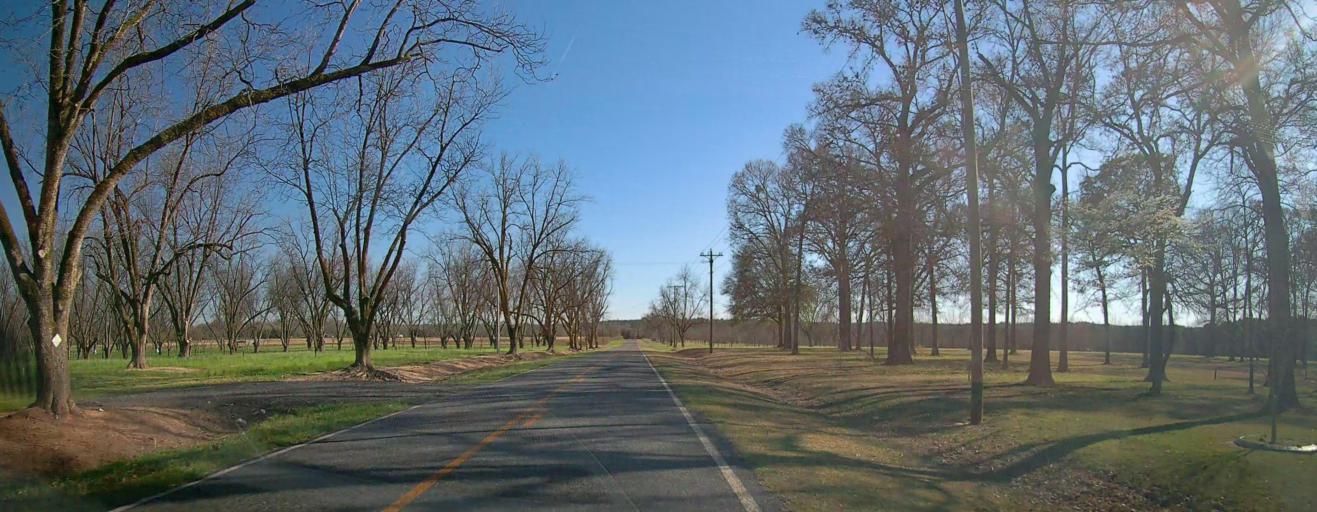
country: US
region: Georgia
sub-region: Peach County
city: Fort Valley
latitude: 32.6014
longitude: -83.8523
